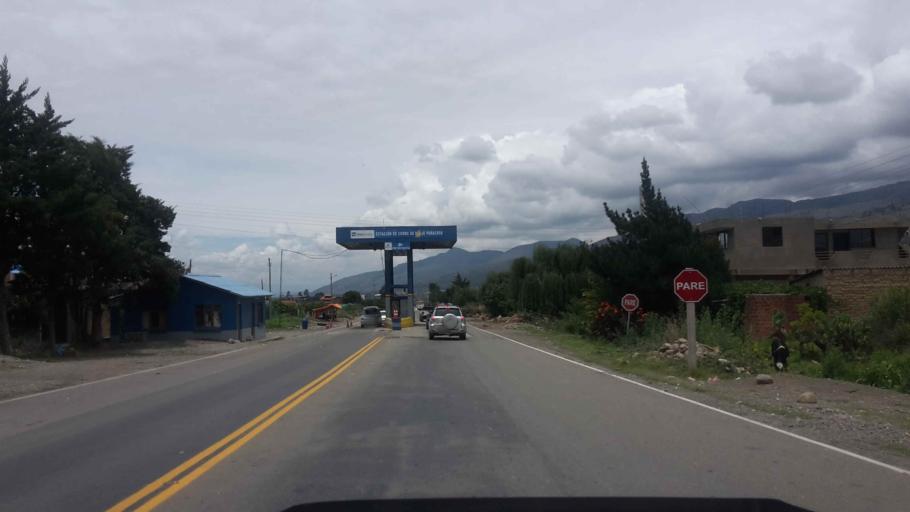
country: BO
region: Cochabamba
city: Punata
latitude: -17.5148
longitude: -65.8260
